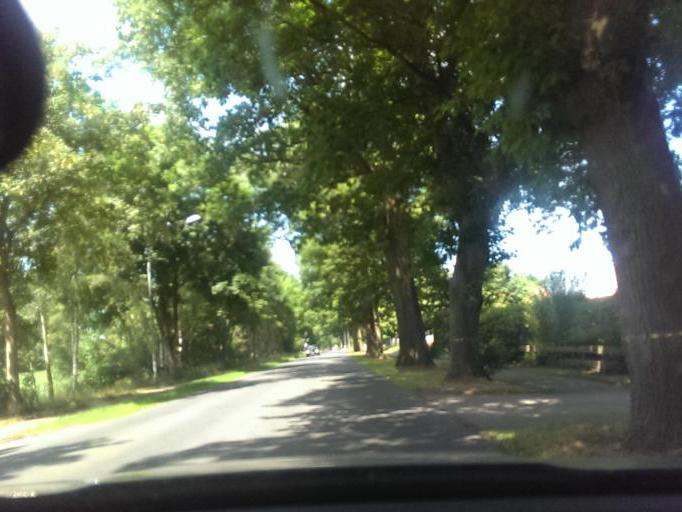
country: DE
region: Lower Saxony
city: Hellwege
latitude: 53.0706
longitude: 9.2504
